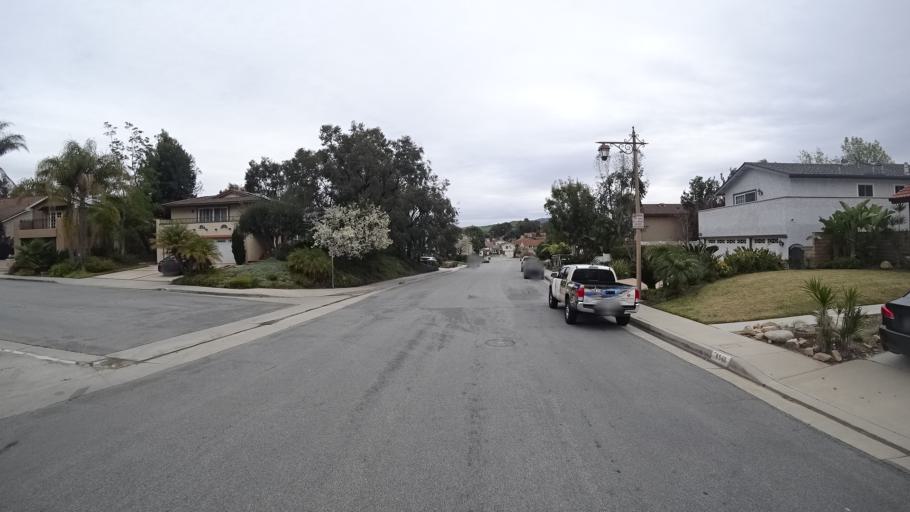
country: US
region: California
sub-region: Orange County
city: Villa Park
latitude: 33.8325
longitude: -117.7603
